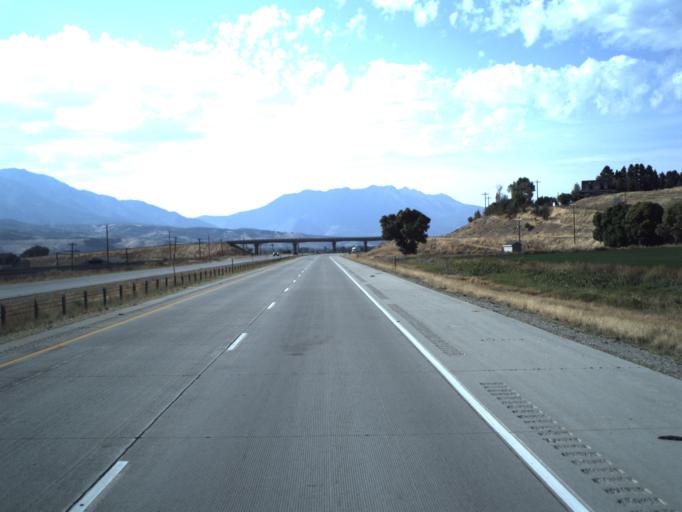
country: US
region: Utah
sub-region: Morgan County
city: Morgan
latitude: 41.0634
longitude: -111.7069
